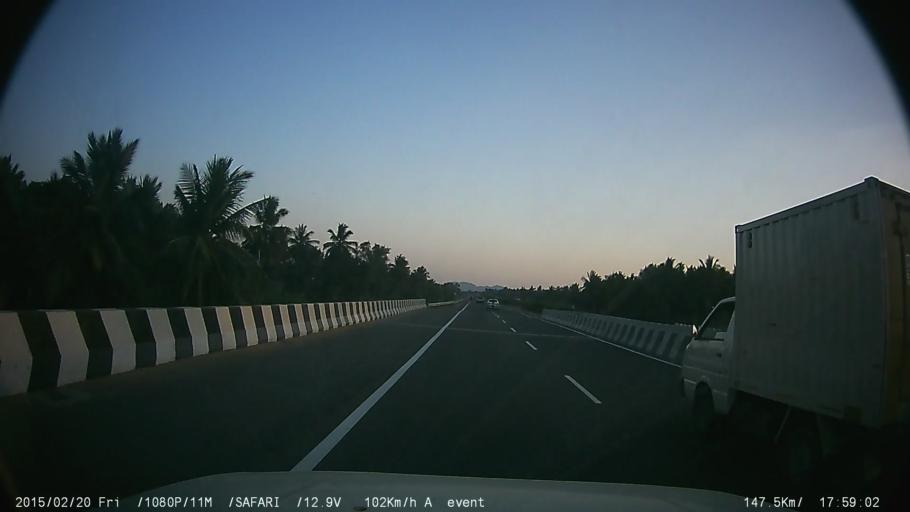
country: IN
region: Tamil Nadu
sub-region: Krishnagiri
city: Kaverippattanam
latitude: 12.4220
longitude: 78.2264
